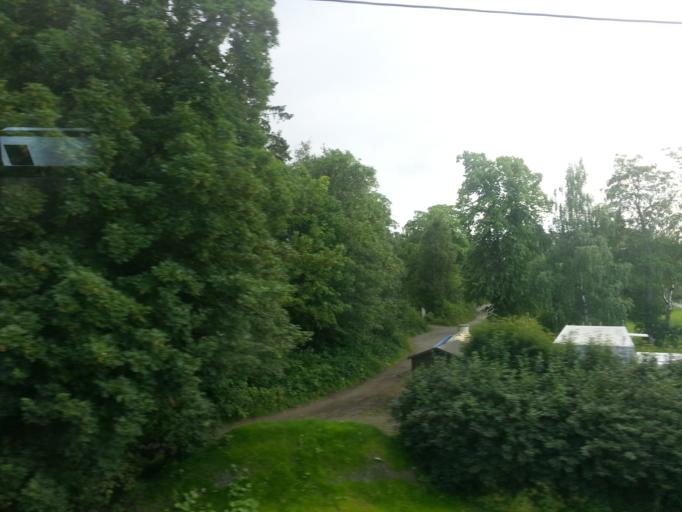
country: NO
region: Sor-Trondelag
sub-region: Trondheim
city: Trondheim
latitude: 63.4407
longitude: 10.4428
